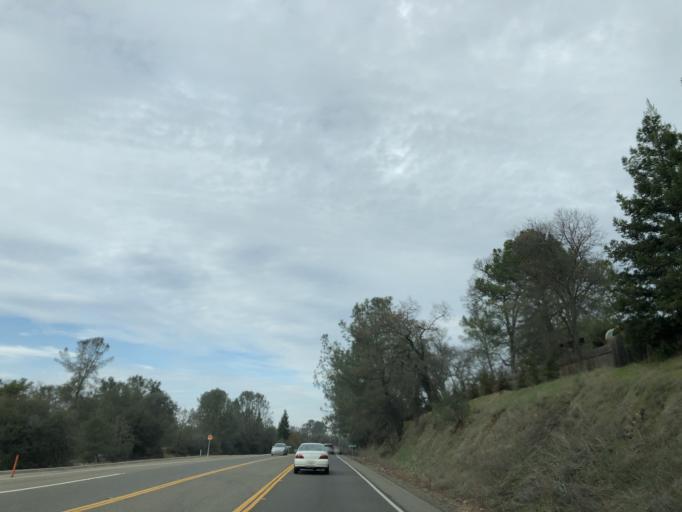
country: US
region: California
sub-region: El Dorado County
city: El Dorado Hills
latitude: 38.6974
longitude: -121.0830
